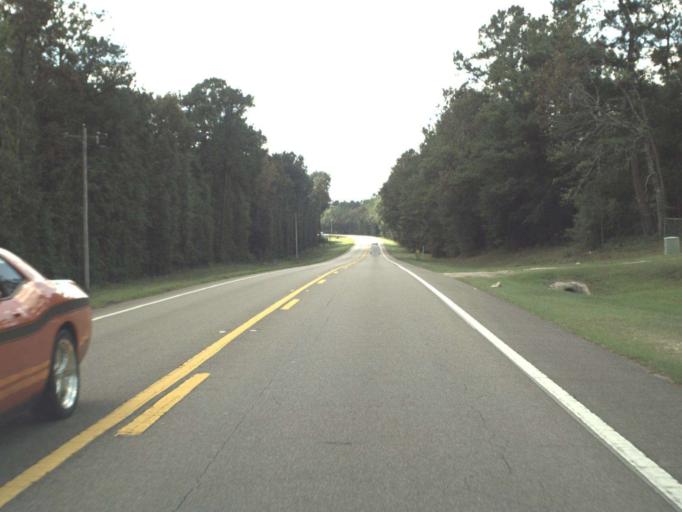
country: US
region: Florida
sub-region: Walton County
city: DeFuniak Springs
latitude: 30.7016
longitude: -85.9350
